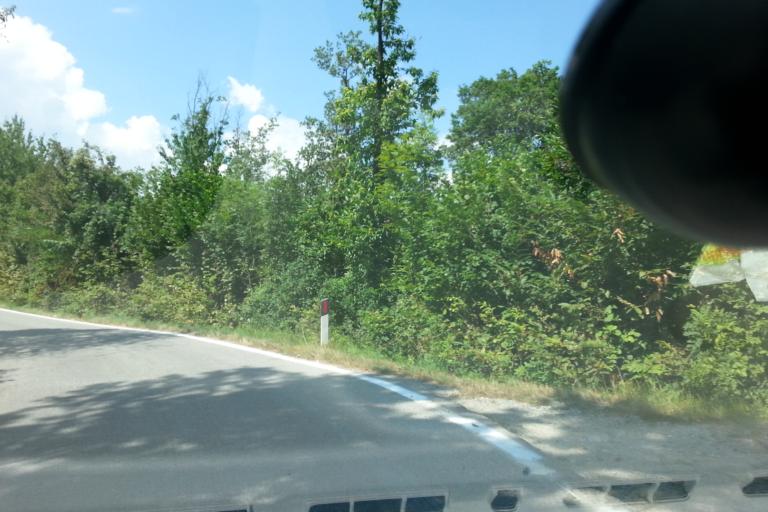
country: IT
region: Piedmont
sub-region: Provincia di Torino
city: Valgioie
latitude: 45.0686
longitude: 7.3698
